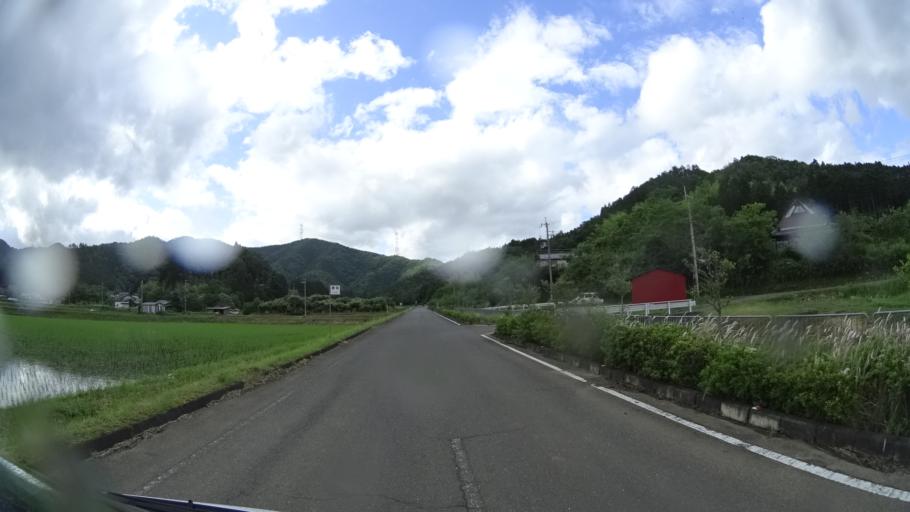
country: JP
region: Kyoto
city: Ayabe
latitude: 35.3477
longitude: 135.1987
